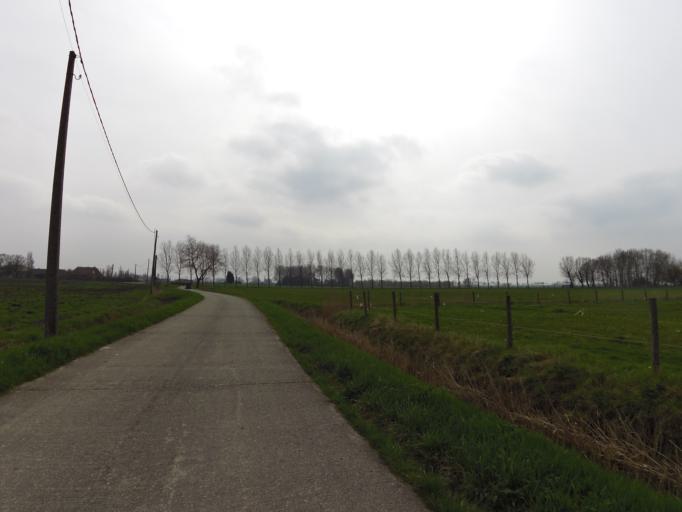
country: BE
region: Flanders
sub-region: Provincie West-Vlaanderen
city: Middelkerke
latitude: 51.1794
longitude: 2.8584
